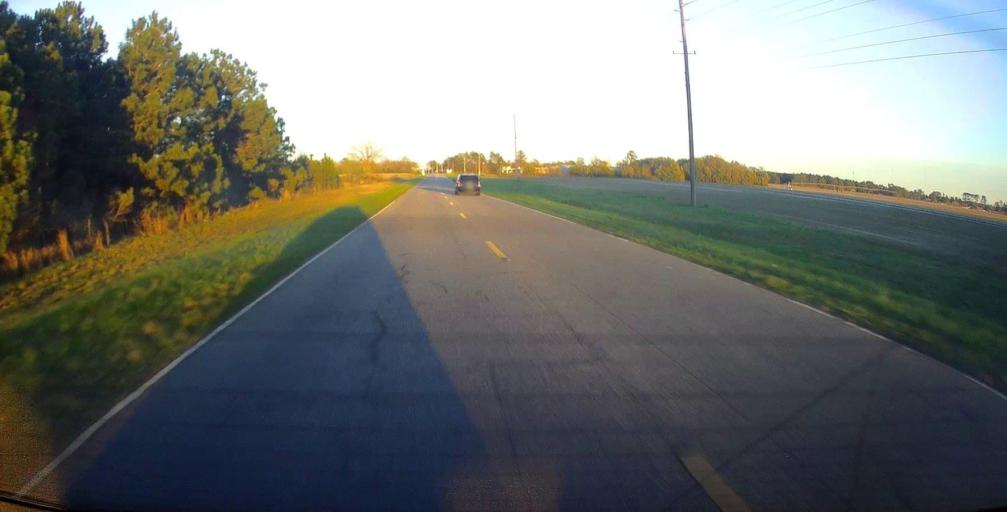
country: US
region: Georgia
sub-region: Crisp County
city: Cordele
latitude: 31.9553
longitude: -83.8023
